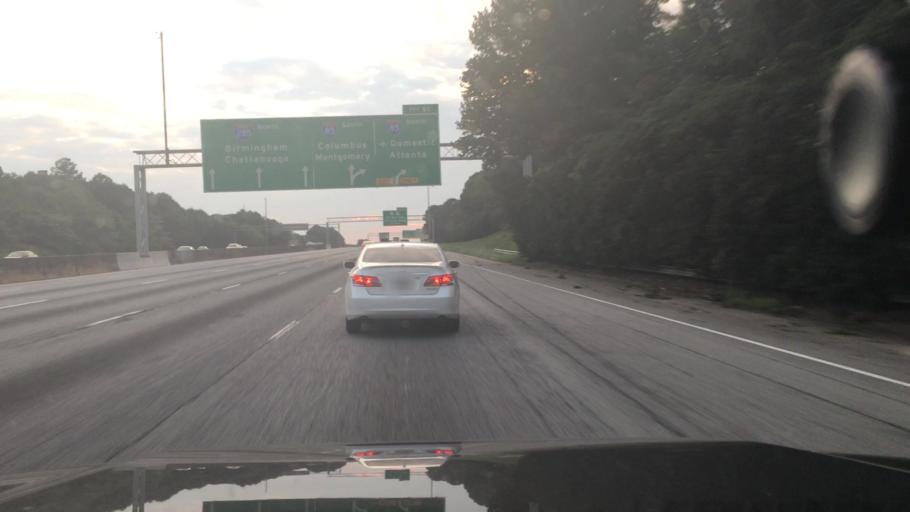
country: US
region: Georgia
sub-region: Fulton County
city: College Park
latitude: 33.6168
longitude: -84.4456
